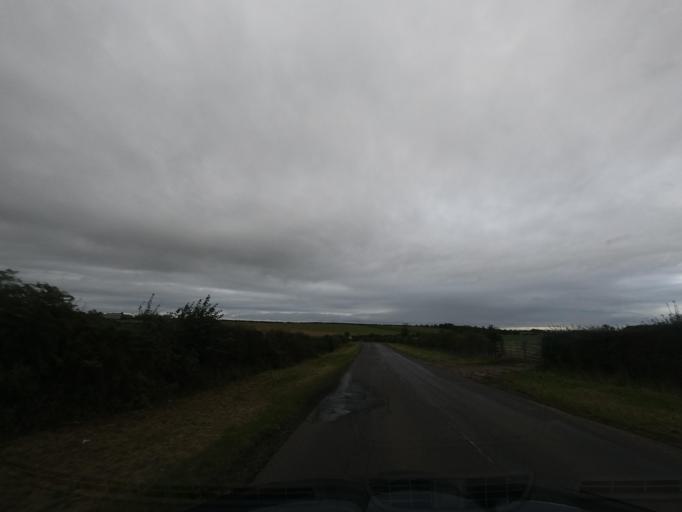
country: GB
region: England
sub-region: Northumberland
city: Ancroft
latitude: 55.7065
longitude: -2.0570
